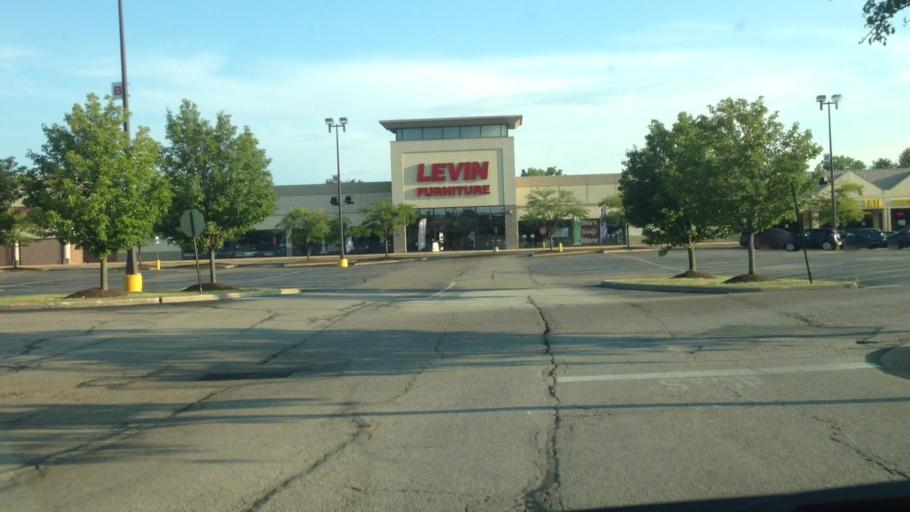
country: US
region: Ohio
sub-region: Summit County
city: Montrose-Ghent
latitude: 41.1325
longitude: -81.6452
